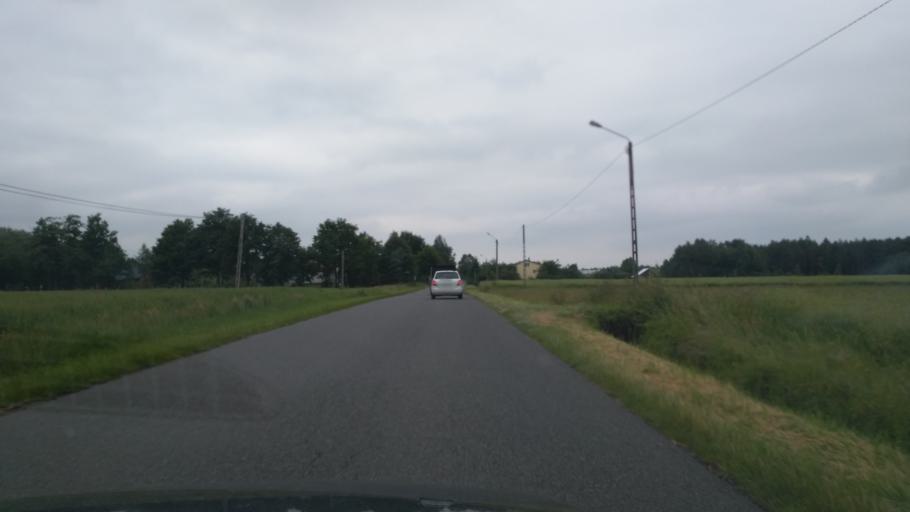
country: PL
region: Subcarpathian Voivodeship
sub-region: Powiat kolbuszowski
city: Niwiska
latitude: 50.1696
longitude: 21.6684
